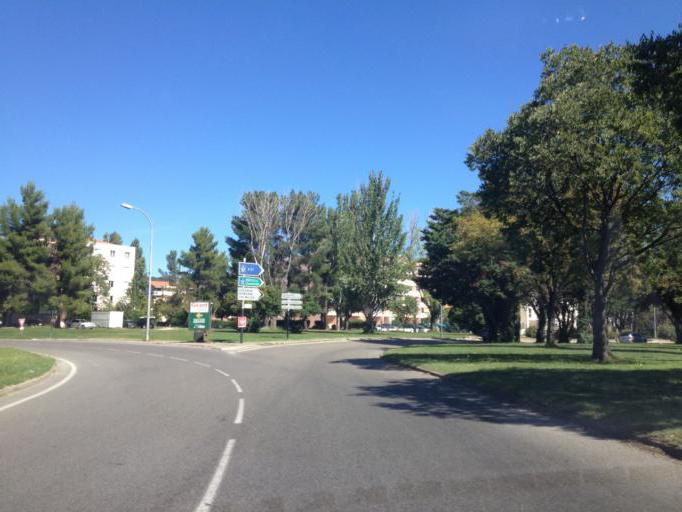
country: FR
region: Provence-Alpes-Cote d'Azur
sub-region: Departement des Bouches-du-Rhone
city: Aix-en-Provence
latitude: 43.5301
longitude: 5.4168
